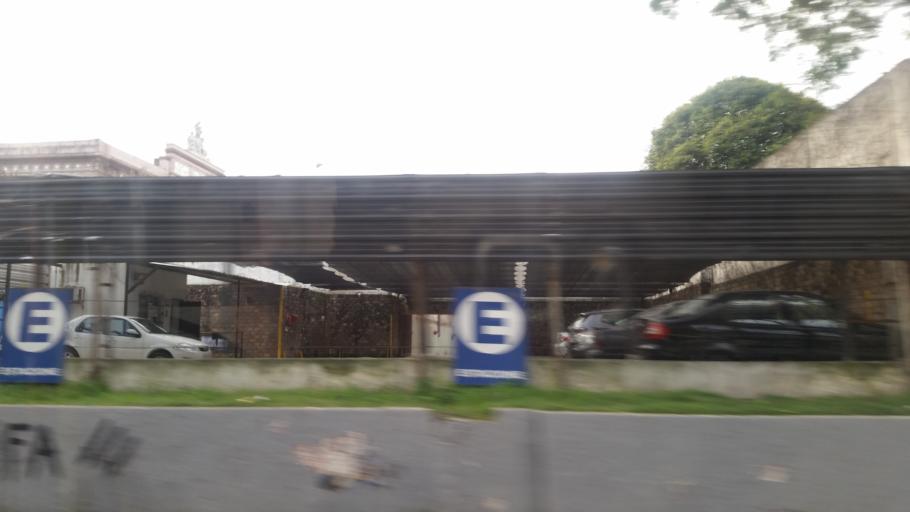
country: AR
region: Buenos Aires F.D.
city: Colegiales
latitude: -34.6072
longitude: -58.4244
